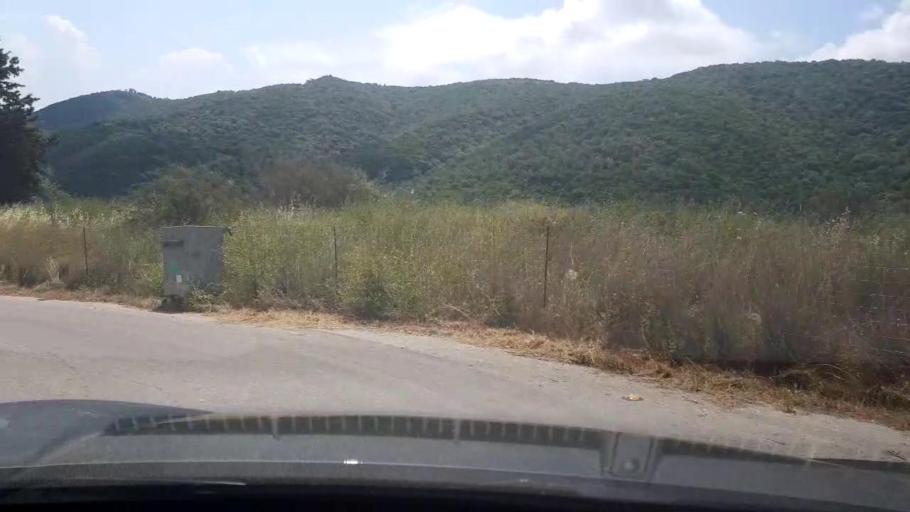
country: GR
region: Ionian Islands
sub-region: Lefkada
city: Nidri
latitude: 38.6432
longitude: 20.6962
